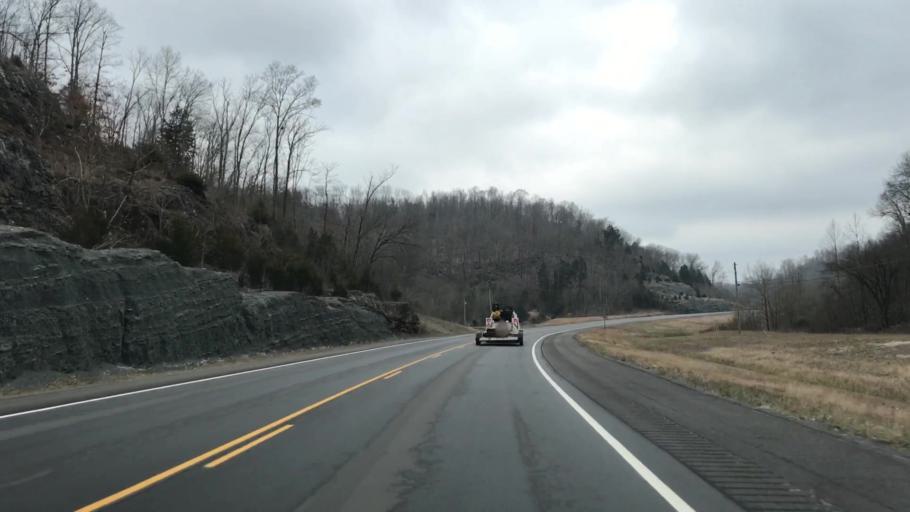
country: US
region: Kentucky
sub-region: Cumberland County
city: Burkesville
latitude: 36.9005
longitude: -85.4301
